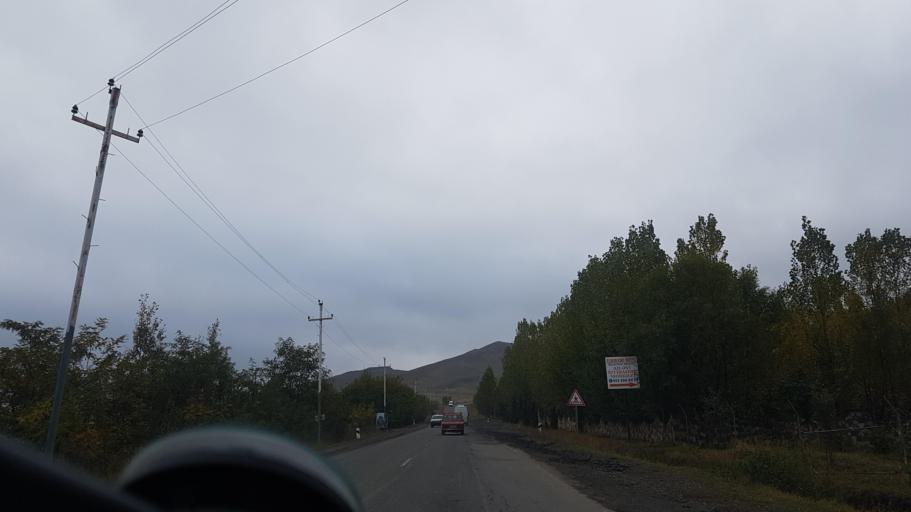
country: AZ
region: Gadabay Rayon
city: Ariqdam
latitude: 40.6306
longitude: 45.8142
